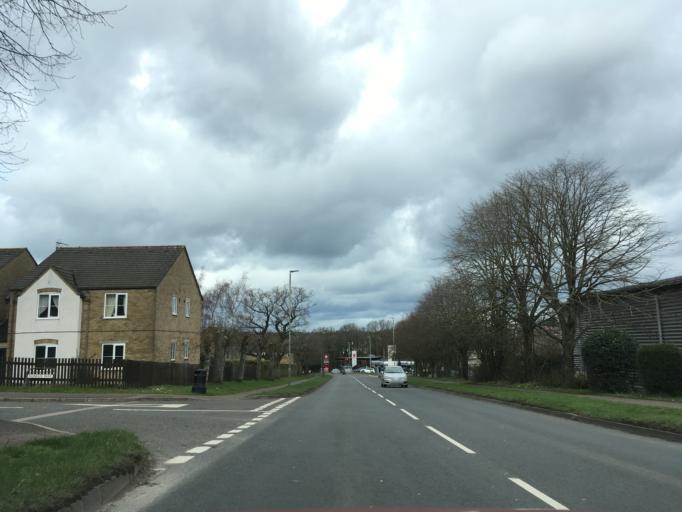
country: GB
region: England
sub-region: Gloucestershire
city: Coleford
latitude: 51.7879
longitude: -2.6135
